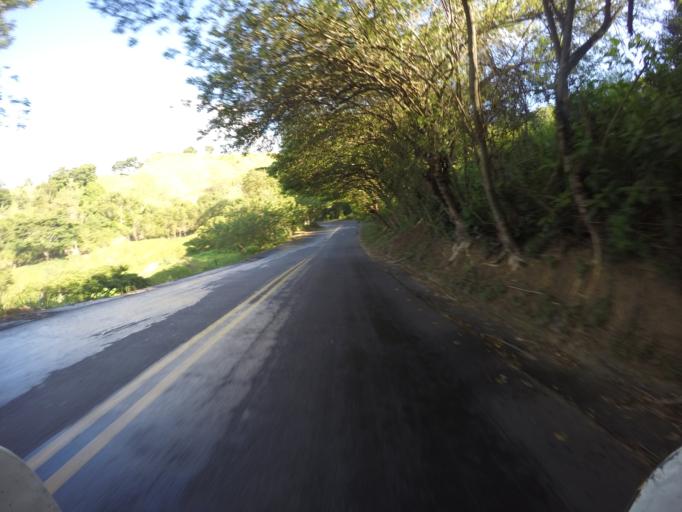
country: CO
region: Valle del Cauca
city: Cartago
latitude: 4.7179
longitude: -75.8618
